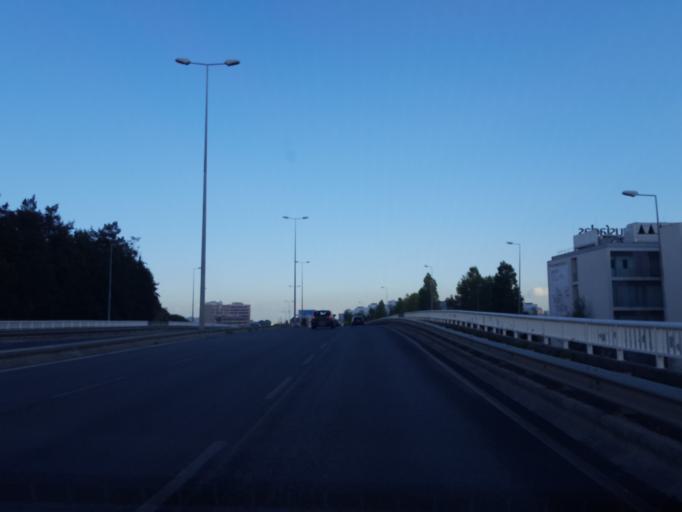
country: PT
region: Lisbon
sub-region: Odivelas
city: Pontinha
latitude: 38.7499
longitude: -9.1803
